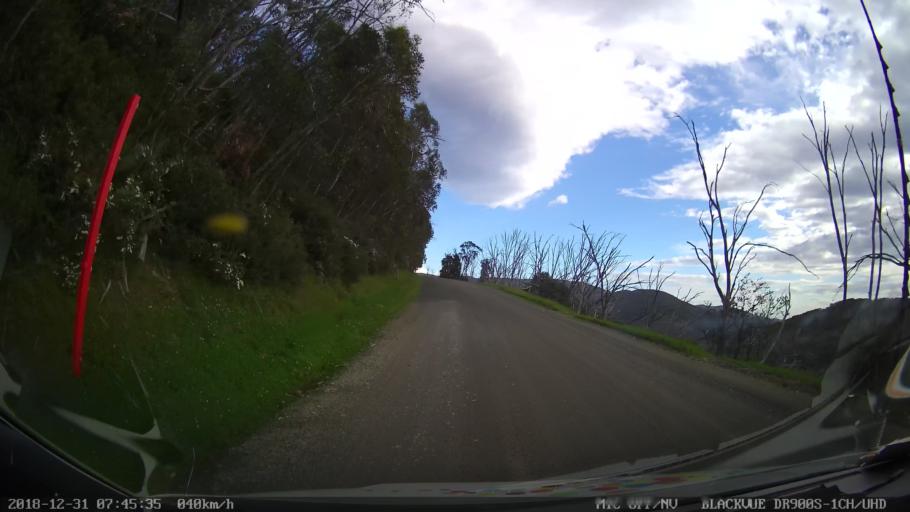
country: AU
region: New South Wales
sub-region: Snowy River
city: Jindabyne
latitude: -36.3633
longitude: 148.4034
